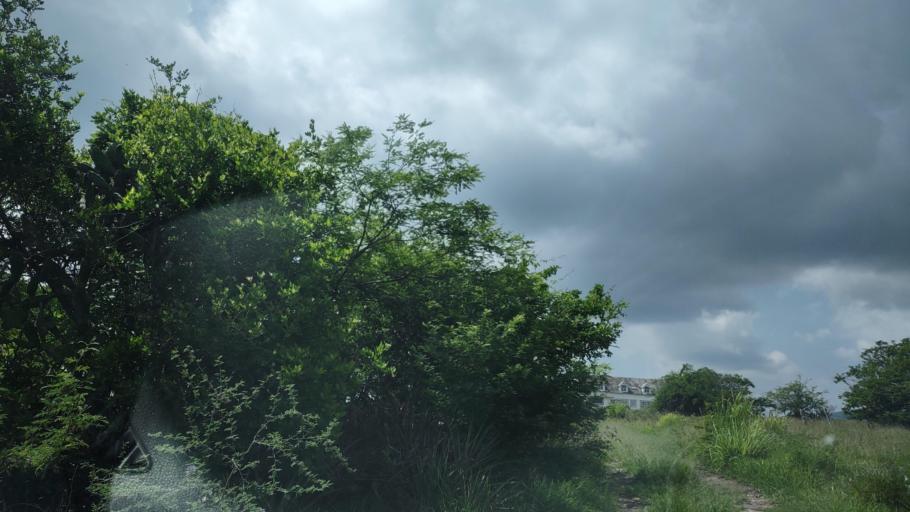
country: MX
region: Veracruz
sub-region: Emiliano Zapata
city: Dos Rios
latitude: 19.4625
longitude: -96.7968
